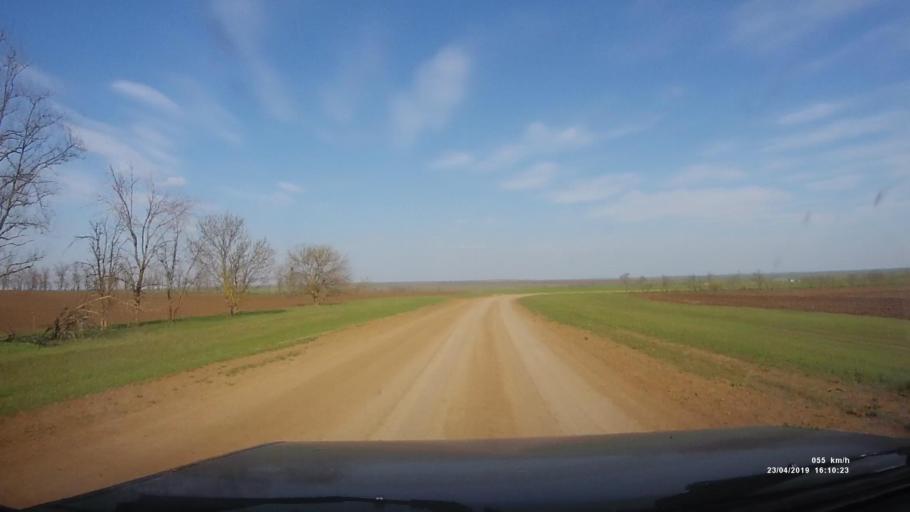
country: RU
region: Rostov
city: Remontnoye
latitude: 46.4815
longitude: 43.1214
